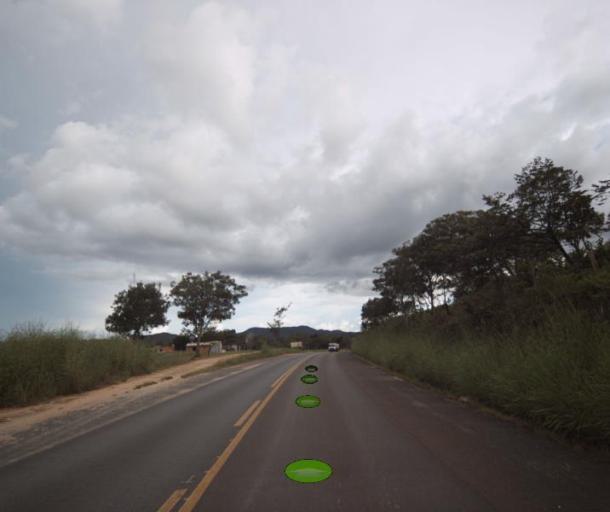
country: BR
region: Goias
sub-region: Niquelandia
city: Niquelandia
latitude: -14.4860
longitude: -48.4886
